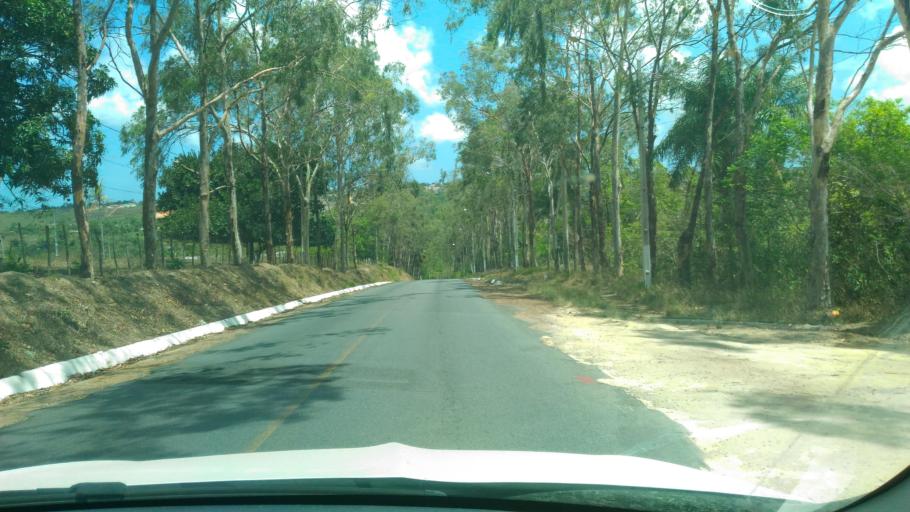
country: BR
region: Paraiba
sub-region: Conde
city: Conde
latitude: -7.2627
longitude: -34.9281
